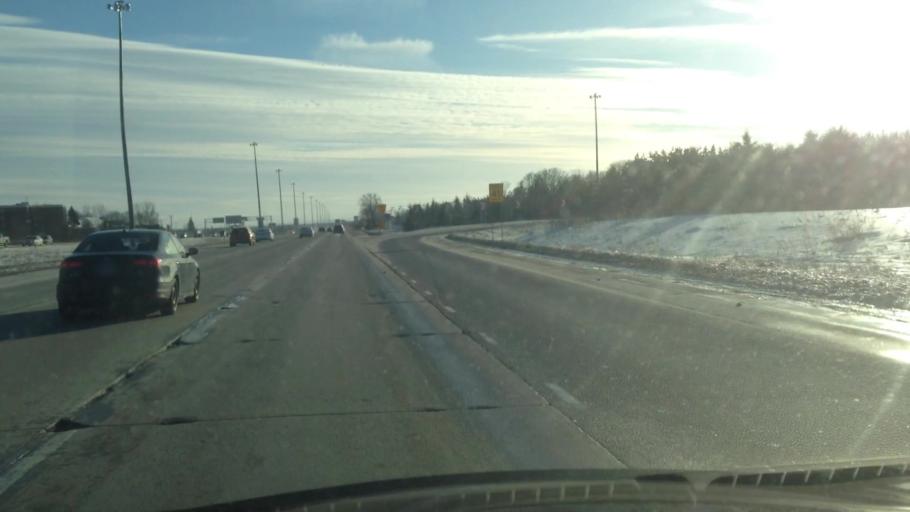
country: CA
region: Quebec
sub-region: Laurentides
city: Saint-Jerome
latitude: 45.7785
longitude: -74.0209
